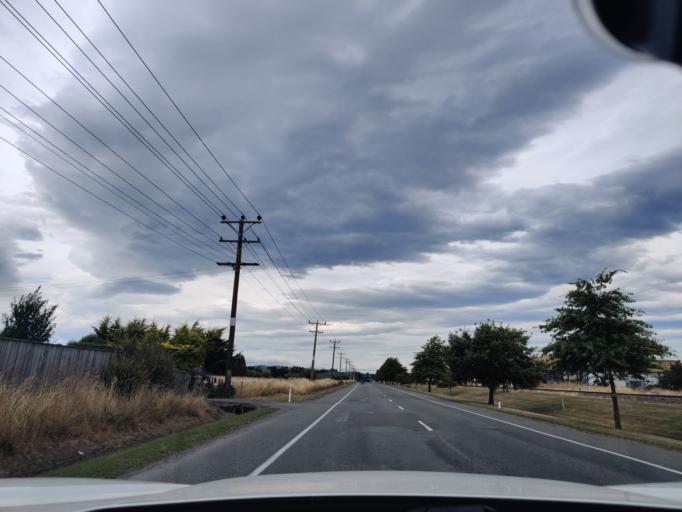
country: NZ
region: Wellington
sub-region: Masterton District
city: Masterton
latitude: -40.9561
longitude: 175.6189
